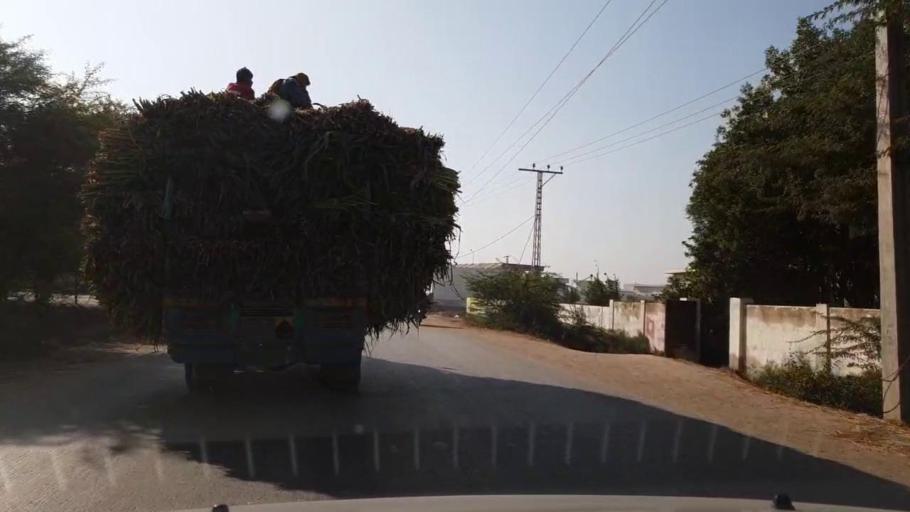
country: PK
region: Sindh
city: Tando Muhammad Khan
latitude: 25.1137
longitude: 68.5267
